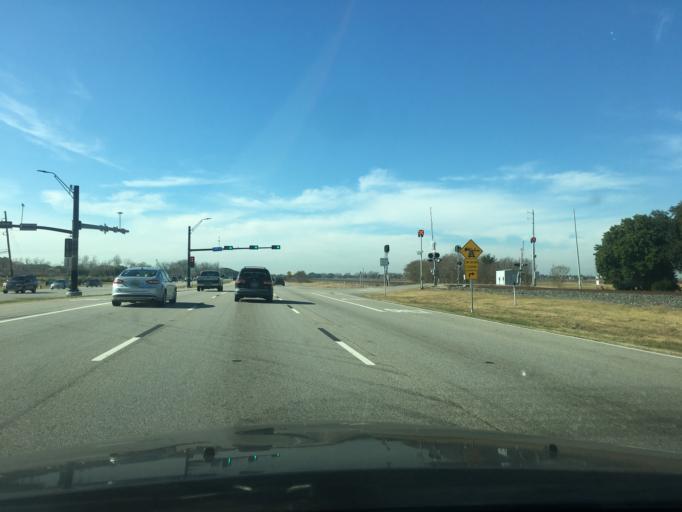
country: US
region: Texas
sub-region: Fort Bend County
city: New Territory
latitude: 29.6087
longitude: -95.6596
